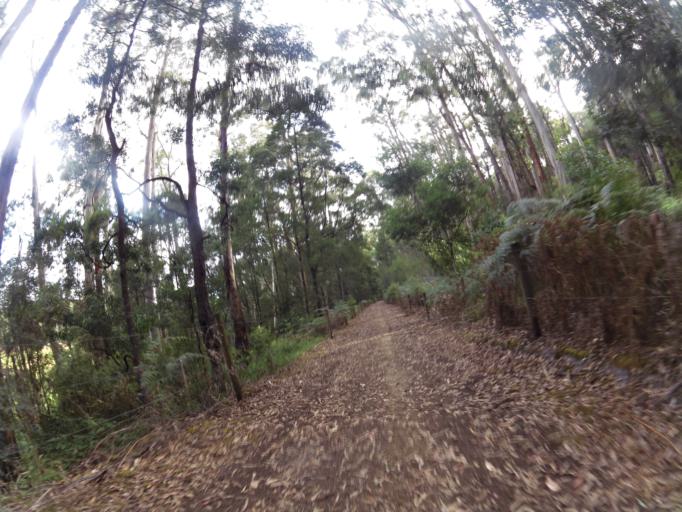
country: AU
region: Victoria
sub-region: Colac-Otway
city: Colac
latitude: -38.4947
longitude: 143.7351
